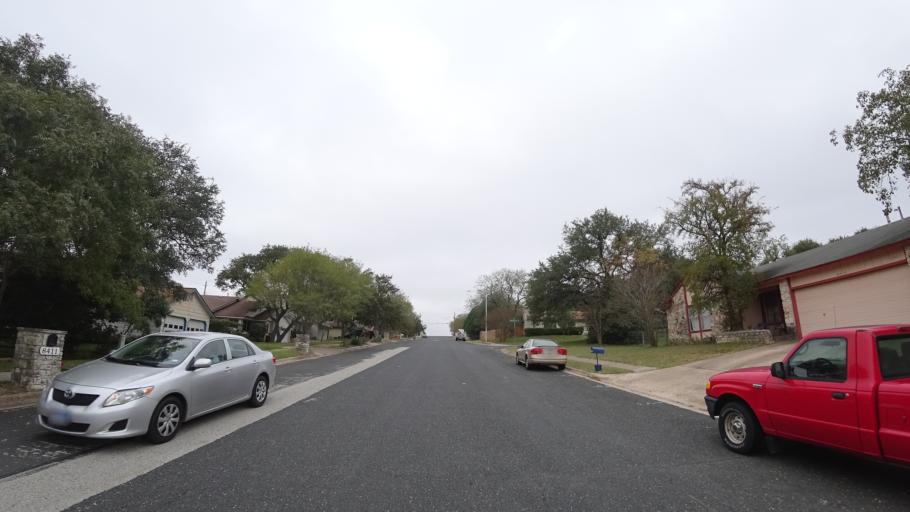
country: US
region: Texas
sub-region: Travis County
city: Barton Creek
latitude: 30.2361
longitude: -97.8997
